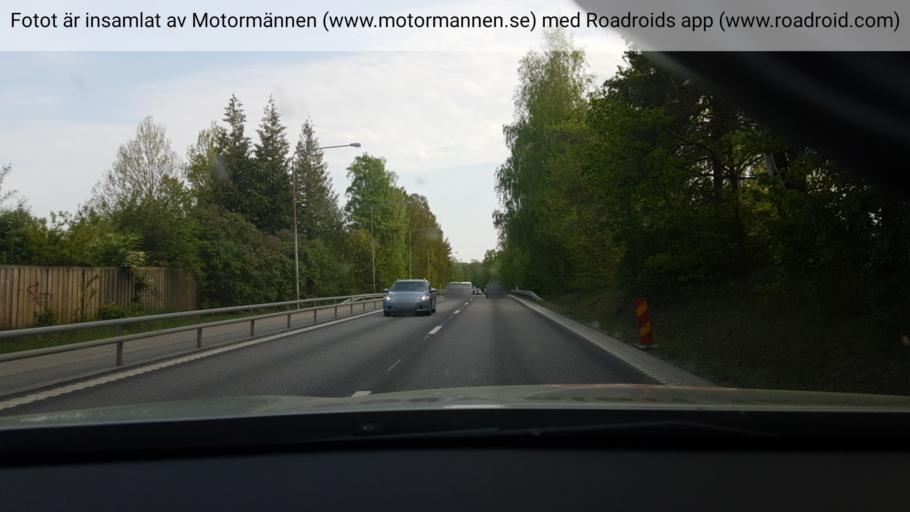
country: SE
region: Stockholm
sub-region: Tyreso Kommun
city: Bollmora
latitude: 59.2210
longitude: 18.2026
